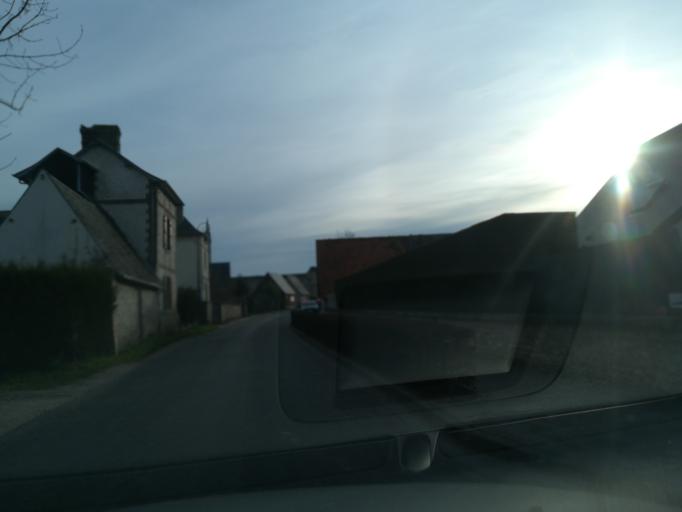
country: FR
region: Haute-Normandie
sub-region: Departement de la Seine-Maritime
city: Saint-Martin-de-Boscherville
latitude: 49.4467
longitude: 0.9646
